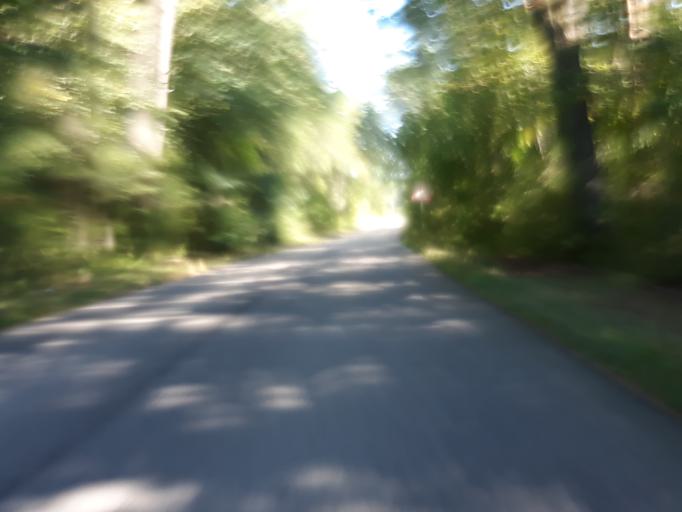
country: DE
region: Baden-Wuerttemberg
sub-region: Karlsruhe Region
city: Gechingen
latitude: 48.6859
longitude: 8.8446
